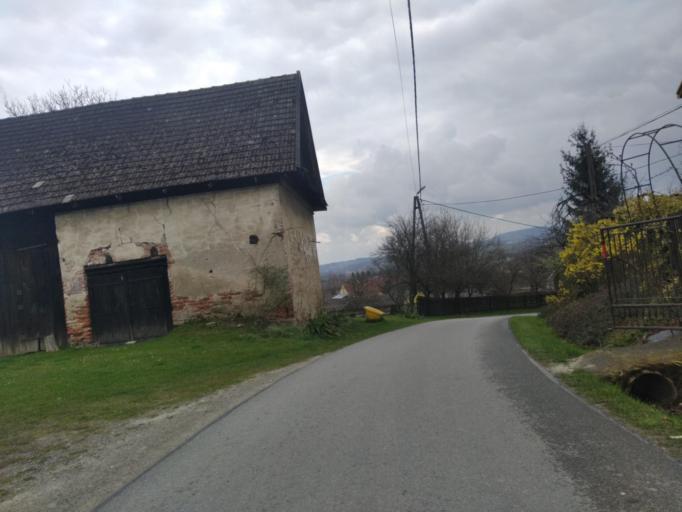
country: PL
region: Subcarpathian Voivodeship
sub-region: Powiat strzyzowski
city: Wisniowa
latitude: 49.8776
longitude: 21.6946
